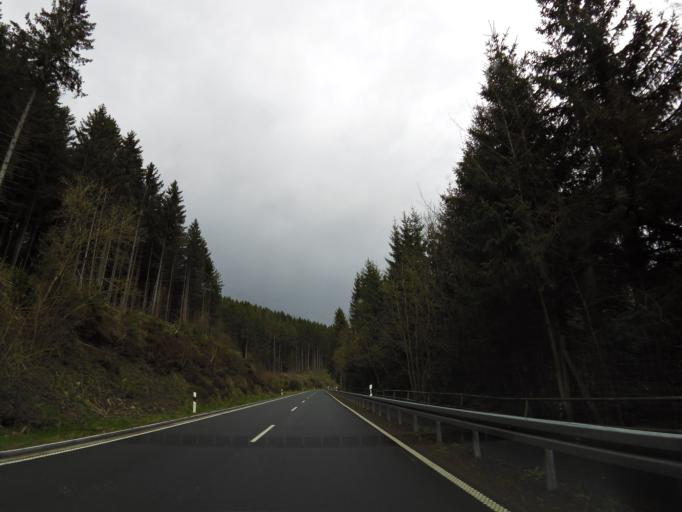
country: DE
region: Lower Saxony
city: Schulenberg im Oberharz
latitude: 51.8207
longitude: 10.4397
